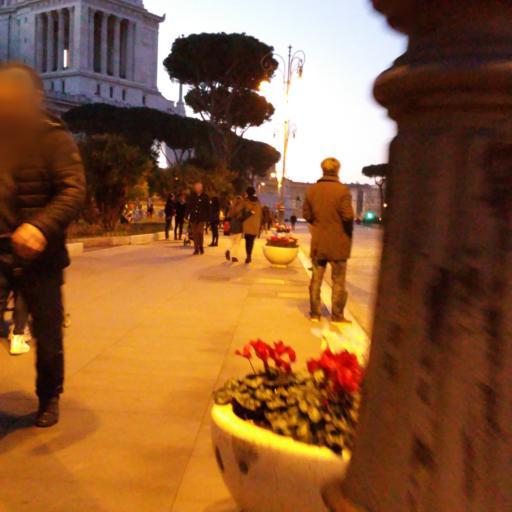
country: IT
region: Latium
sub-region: Citta metropolitana di Roma Capitale
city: Rome
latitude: 41.8938
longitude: 12.4860
